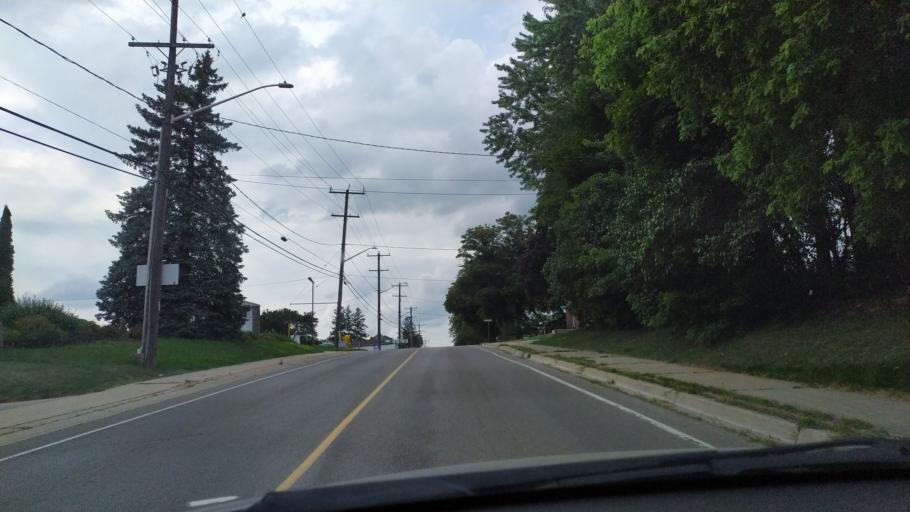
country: CA
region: Ontario
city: Kitchener
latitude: 43.3497
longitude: -80.5371
